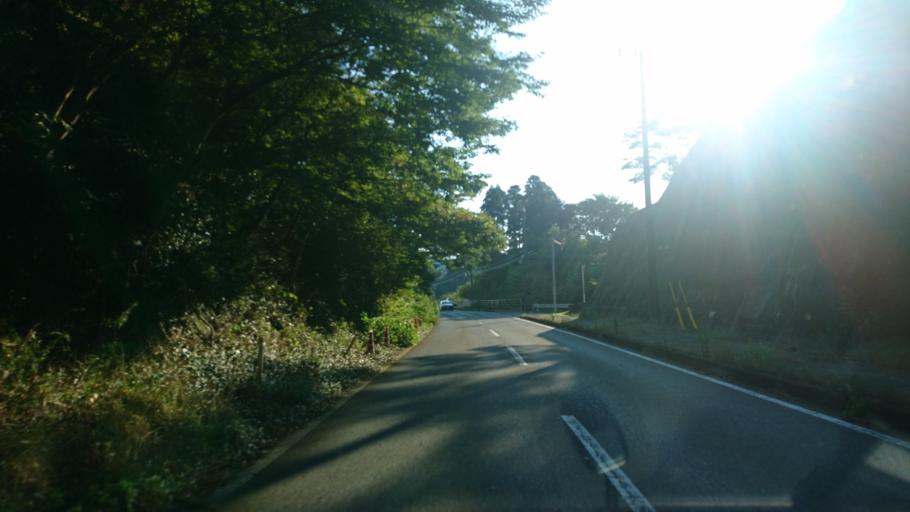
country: JP
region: Chiba
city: Kawaguchi
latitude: 35.2073
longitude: 140.0232
